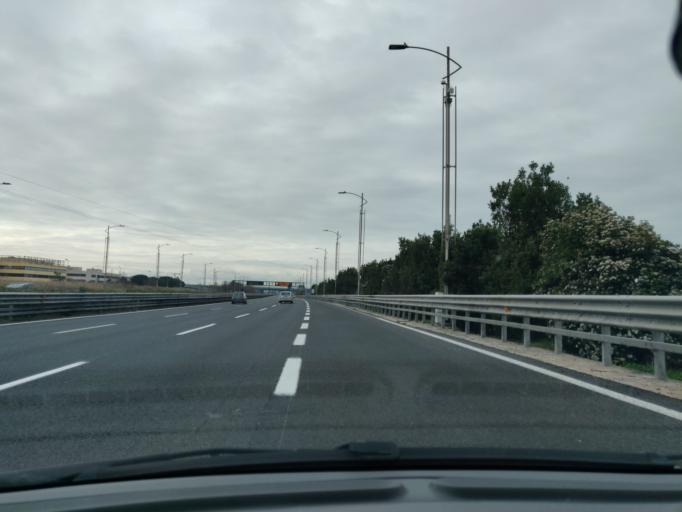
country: IT
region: Latium
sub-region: Citta metropolitana di Roma Capitale
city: Npp 23 (Parco Leonardo)
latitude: 41.8086
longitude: 12.3061
